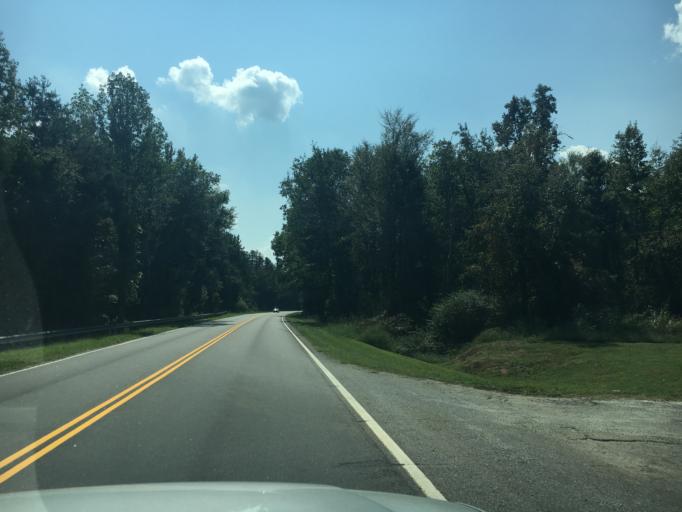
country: US
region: Georgia
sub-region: Hart County
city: Hartwell
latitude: 34.3814
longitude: -82.8110
